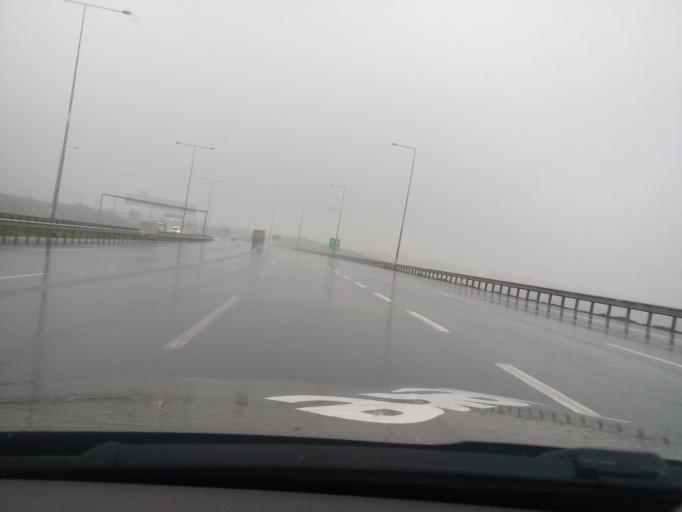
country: TR
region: Istanbul
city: Basaksehir
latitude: 41.1326
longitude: 28.8042
